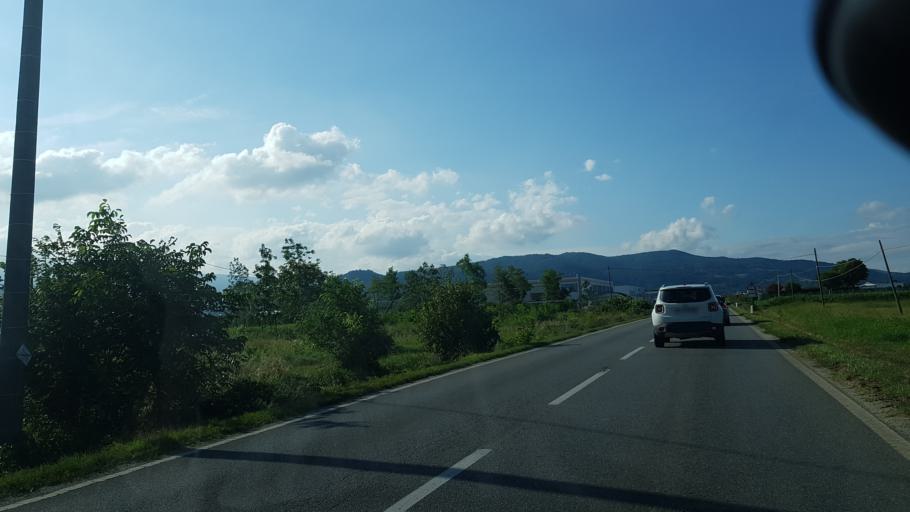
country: IT
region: Piedmont
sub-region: Provincia di Cuneo
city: Busca
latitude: 44.4932
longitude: 7.4965
